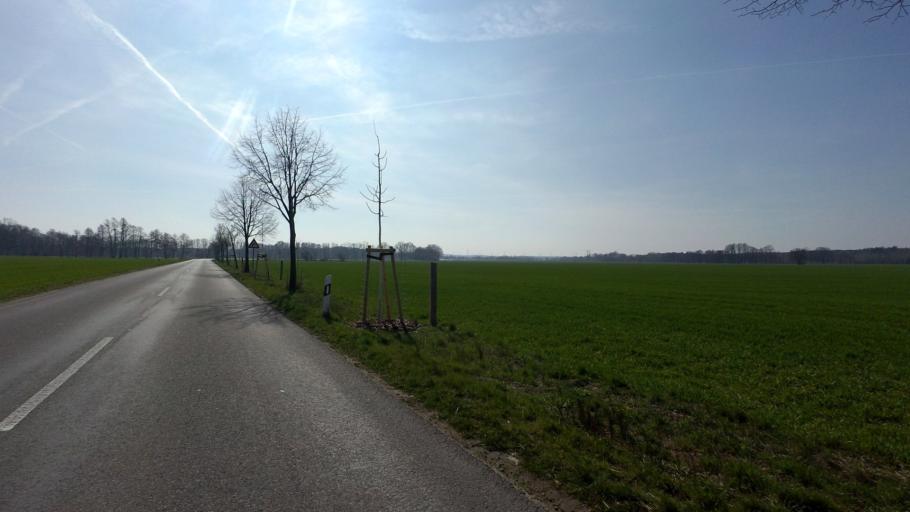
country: DE
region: Brandenburg
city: Drahnsdorf
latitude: 51.9297
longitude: 13.5954
